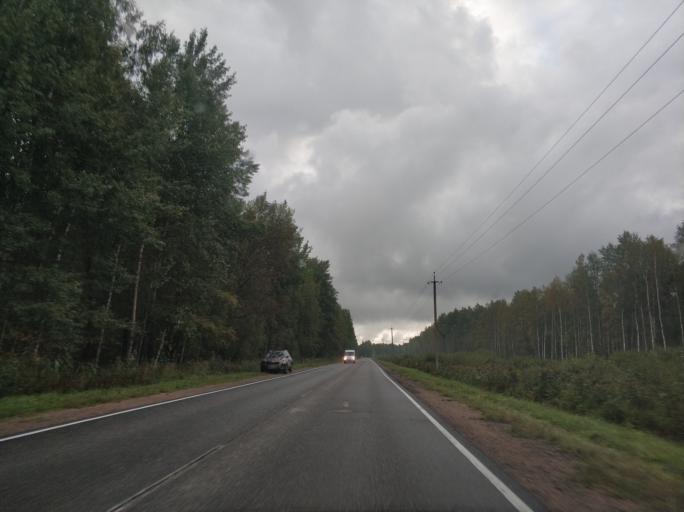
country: RU
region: Leningrad
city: Borisova Griva
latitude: 60.1090
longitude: 30.9605
